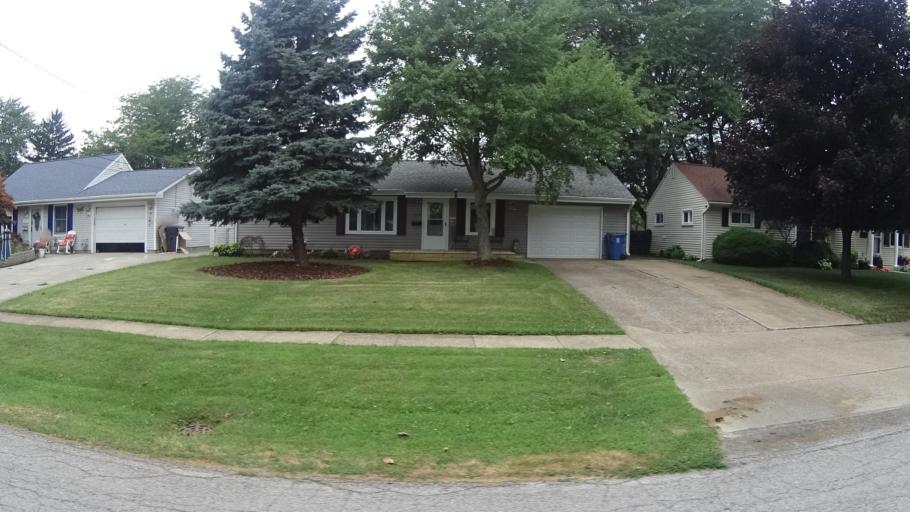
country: US
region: Ohio
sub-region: Erie County
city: Sandusky
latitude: 41.4390
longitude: -82.7640
